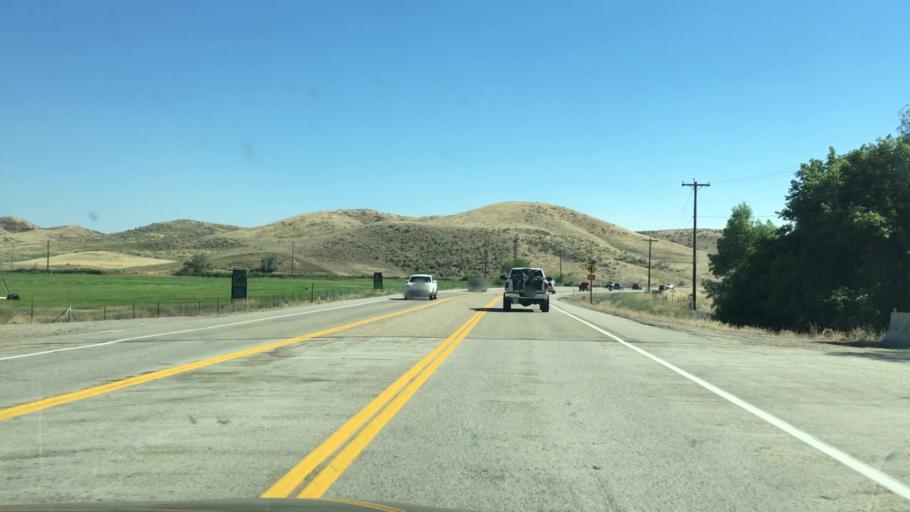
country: US
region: Idaho
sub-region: Ada County
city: Eagle
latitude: 43.7324
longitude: -116.3042
